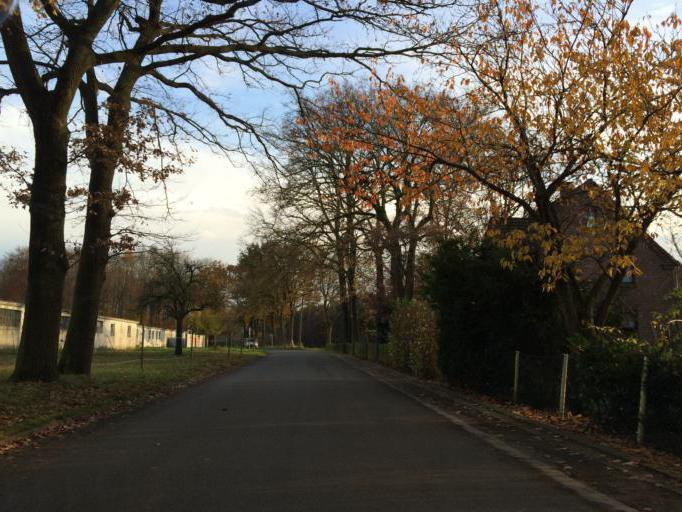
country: DE
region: North Rhine-Westphalia
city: Marl
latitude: 51.6734
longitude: 7.0665
